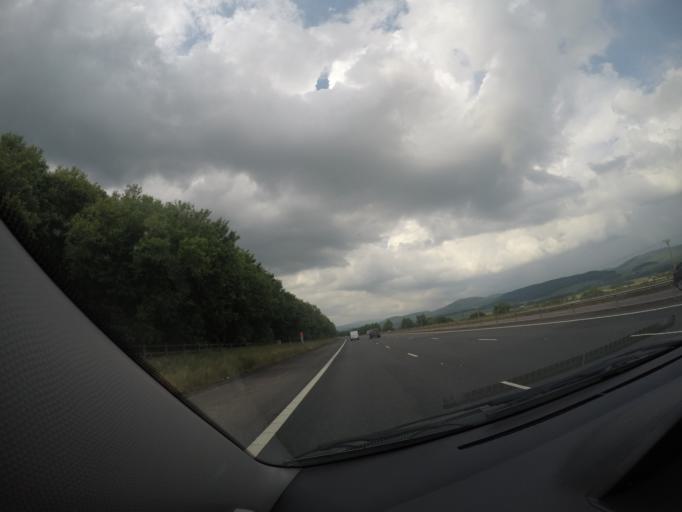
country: GB
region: Scotland
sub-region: Dumfries and Galloway
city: Moffat
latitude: 55.2444
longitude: -3.4093
